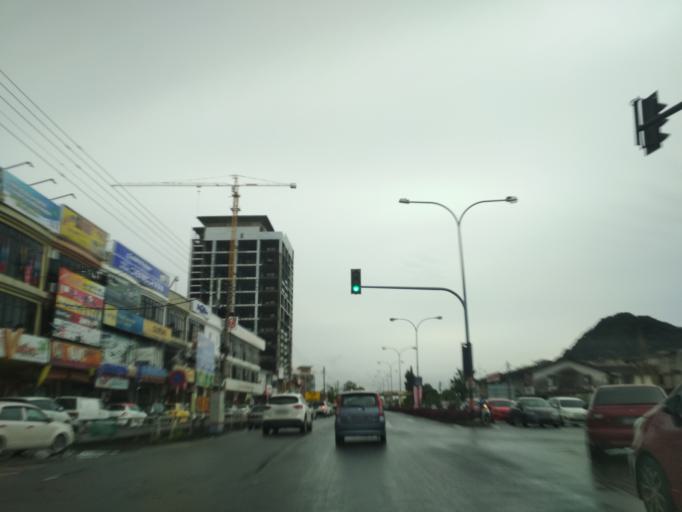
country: MY
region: Perlis
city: Kangar
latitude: 6.4363
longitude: 100.1948
